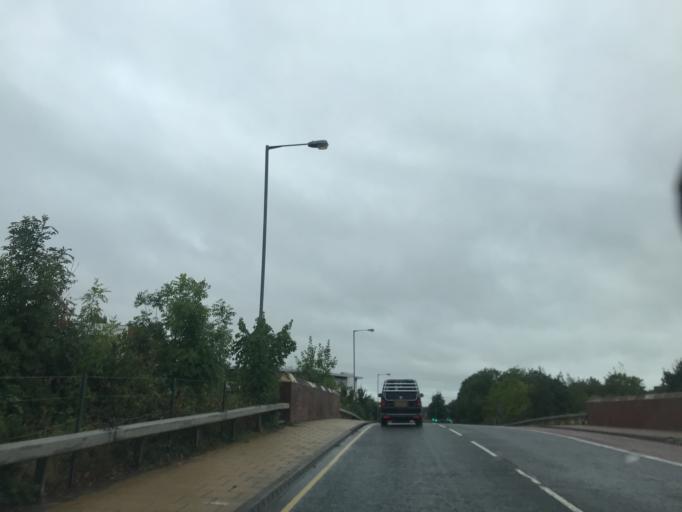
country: GB
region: England
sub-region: Buckinghamshire
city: Aylesbury
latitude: 51.8157
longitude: -0.8224
